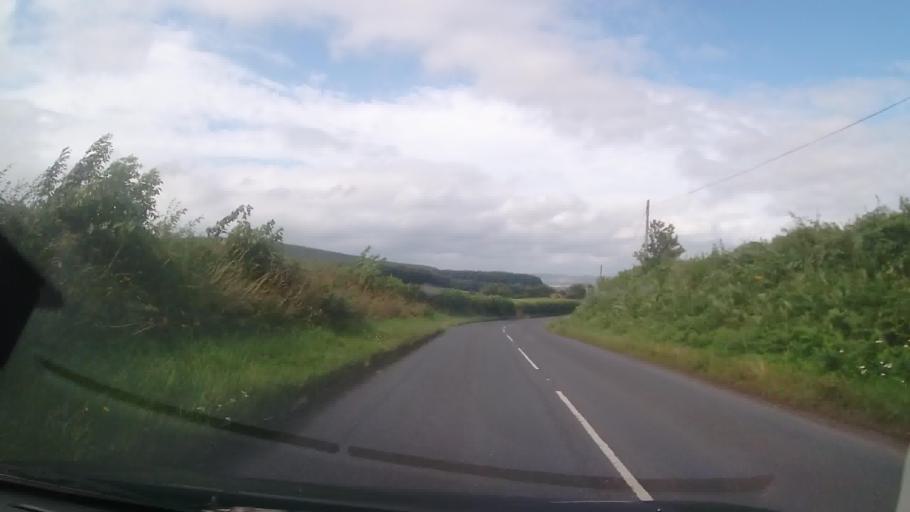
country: GB
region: England
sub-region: Shropshire
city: Acton
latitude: 52.4480
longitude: -3.0307
